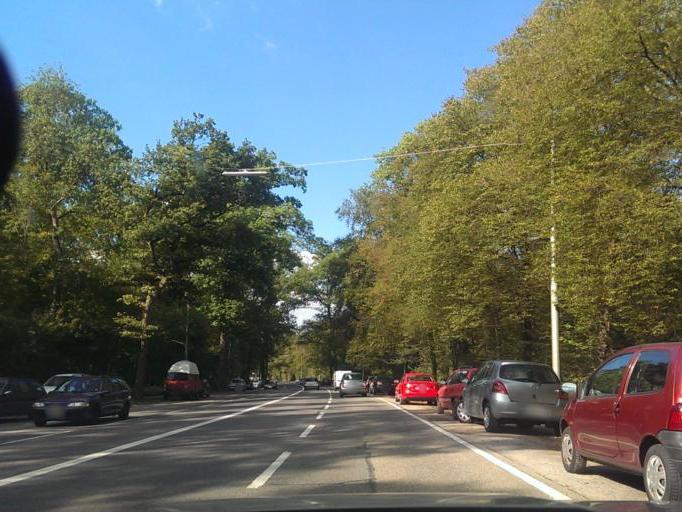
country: DE
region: Baden-Wuerttemberg
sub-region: Karlsruhe Region
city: Karlsruhe
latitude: 49.0170
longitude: 8.4179
